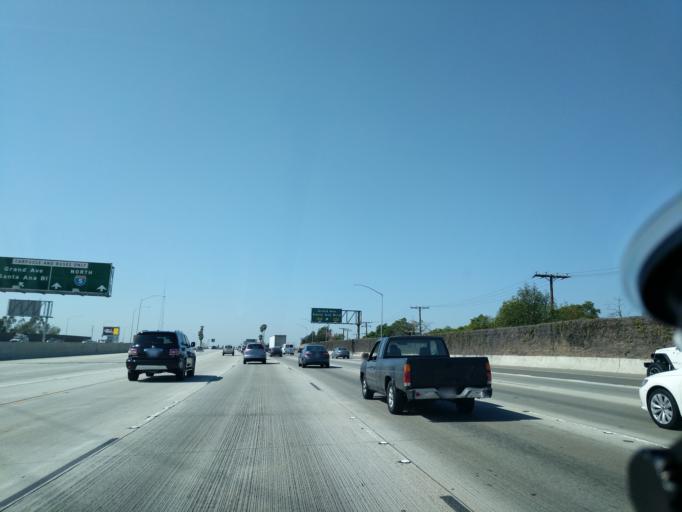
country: US
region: California
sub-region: Orange County
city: Tustin
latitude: 33.7528
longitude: -117.8469
